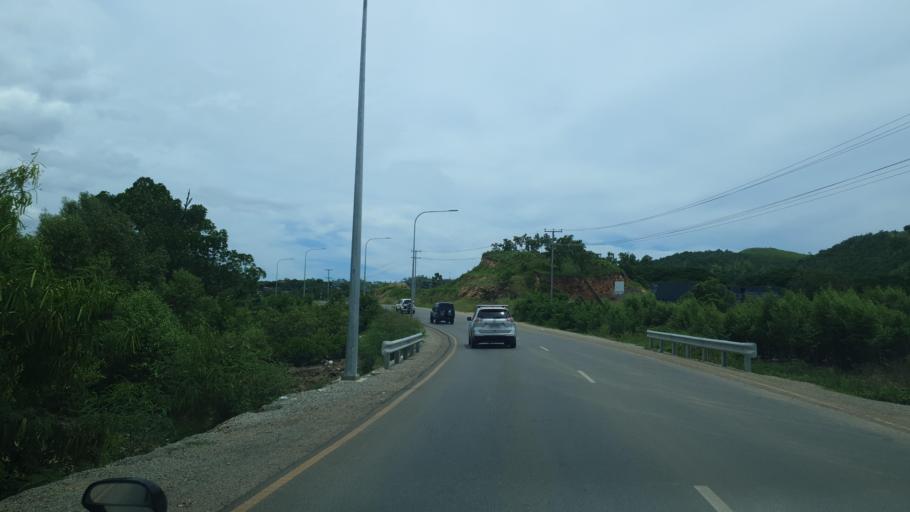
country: PG
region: National Capital
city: Port Moresby
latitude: -9.5029
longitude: 147.2351
